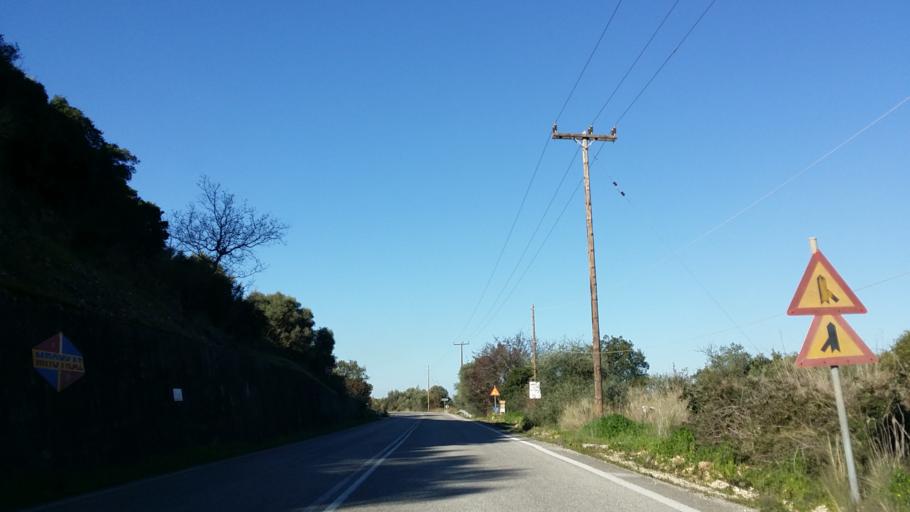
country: GR
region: West Greece
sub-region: Nomos Aitolias kai Akarnanias
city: Amfilochia
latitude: 38.8648
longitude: 21.0762
